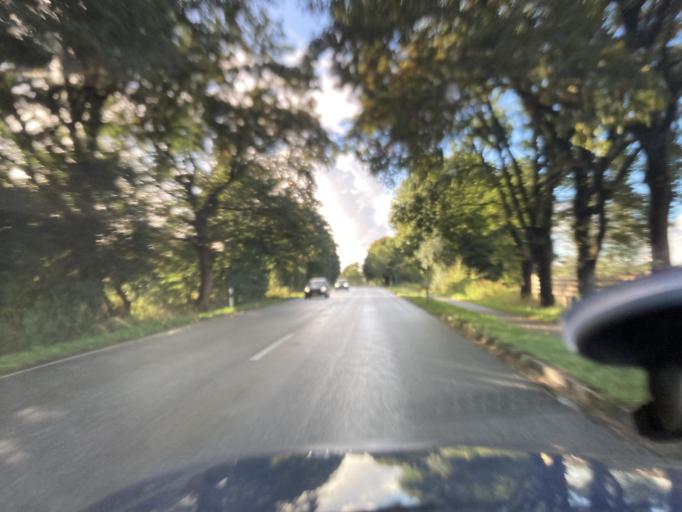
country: DE
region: Schleswig-Holstein
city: Gaushorn
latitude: 54.1956
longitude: 9.2187
